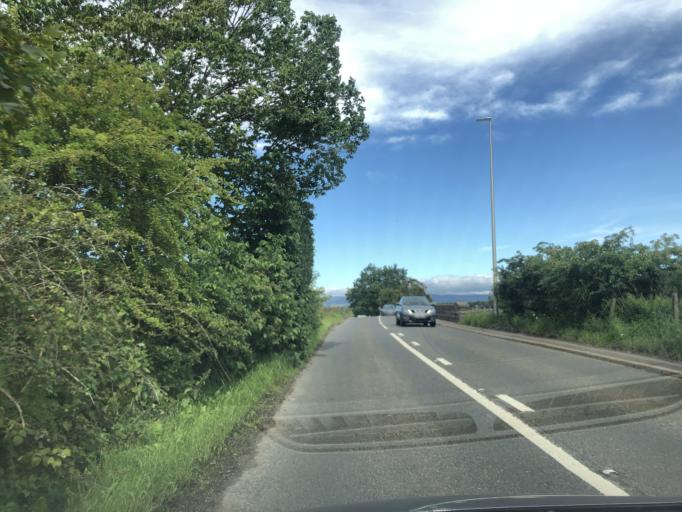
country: GB
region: Scotland
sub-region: Angus
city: Forfar
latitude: 56.6533
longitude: -2.8916
